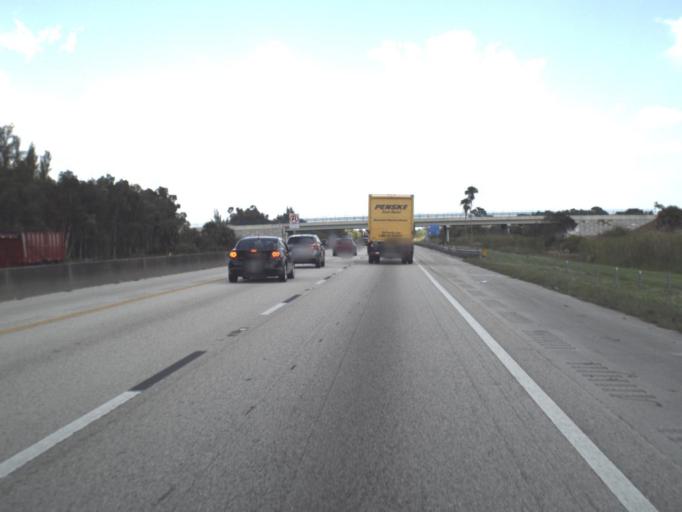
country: US
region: Florida
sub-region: Palm Beach County
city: Schall Circle
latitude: 26.7335
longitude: -80.1351
